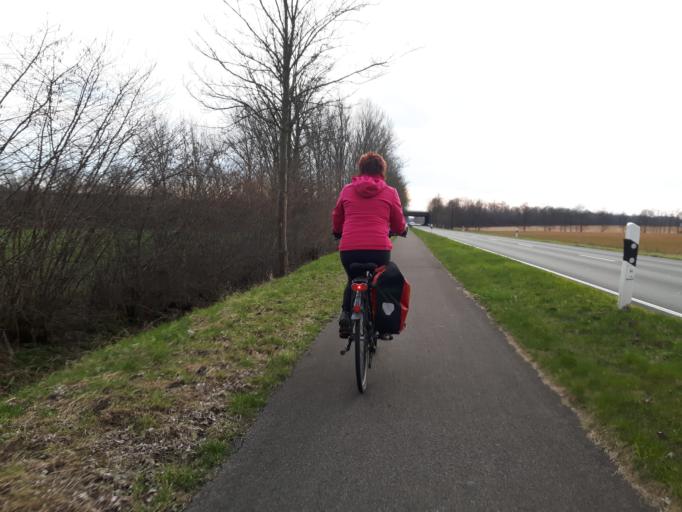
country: DE
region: North Rhine-Westphalia
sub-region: Regierungsbezirk Munster
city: Senden
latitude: 51.9049
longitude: 7.4474
